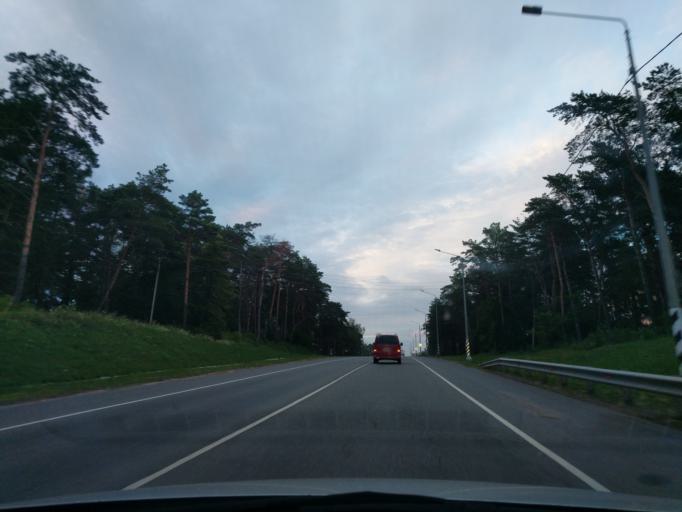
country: RU
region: Kaluga
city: Obninsk
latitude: 55.0627
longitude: 36.5918
